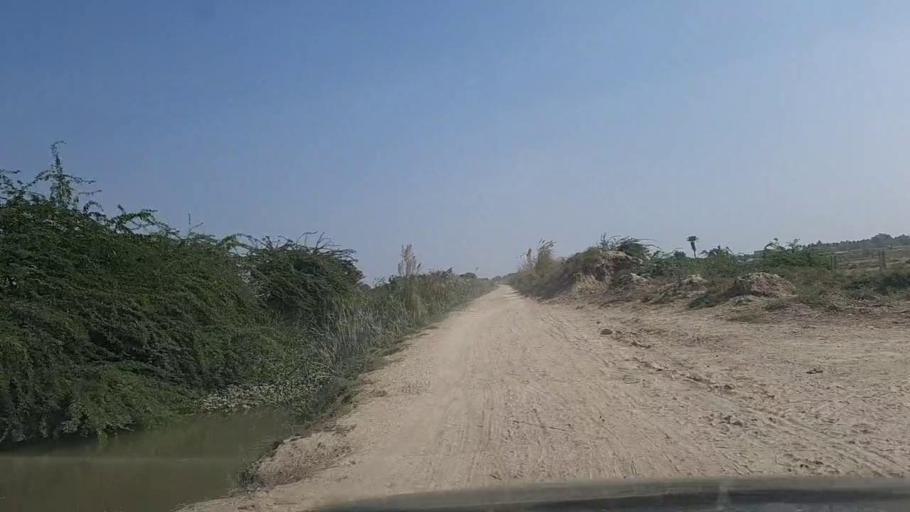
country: PK
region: Sindh
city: Gharo
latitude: 24.7134
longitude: 67.5853
